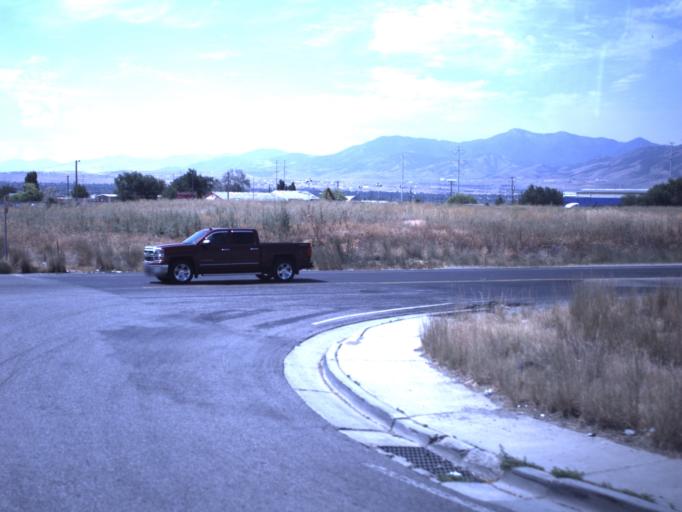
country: US
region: Utah
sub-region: Salt Lake County
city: West Valley City
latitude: 40.7232
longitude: -112.0250
